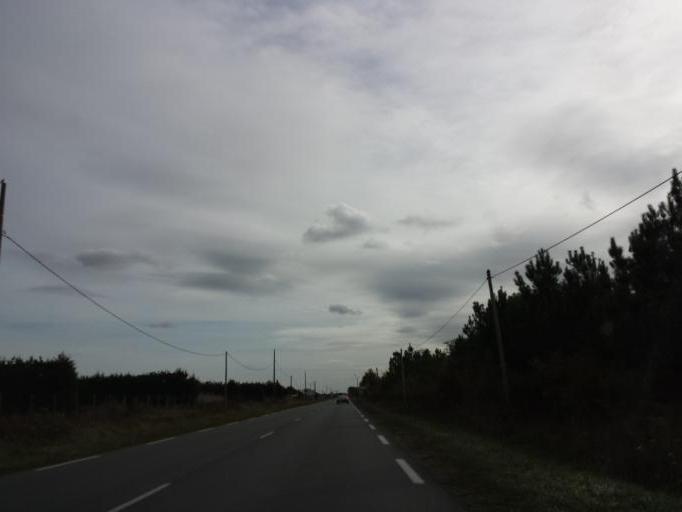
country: FR
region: Aquitaine
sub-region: Departement de la Gironde
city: Marcheprime
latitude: 44.7733
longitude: -0.9280
